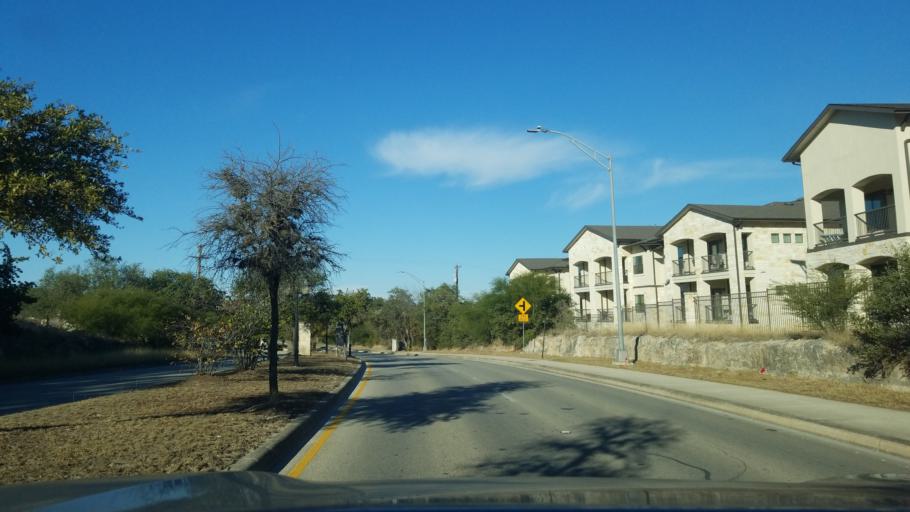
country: US
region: Texas
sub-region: Bexar County
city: Hollywood Park
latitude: 29.6194
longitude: -98.4760
